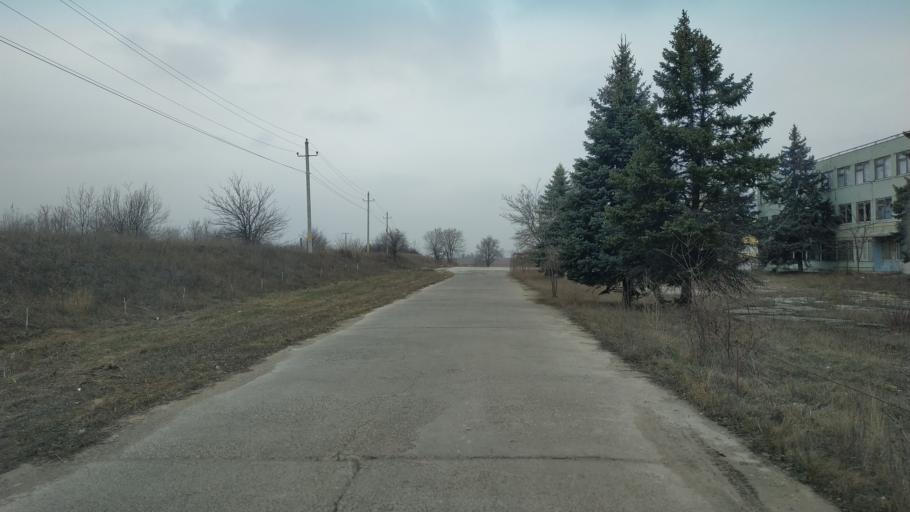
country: MD
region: Chisinau
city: Singera
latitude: 46.9123
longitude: 29.0057
